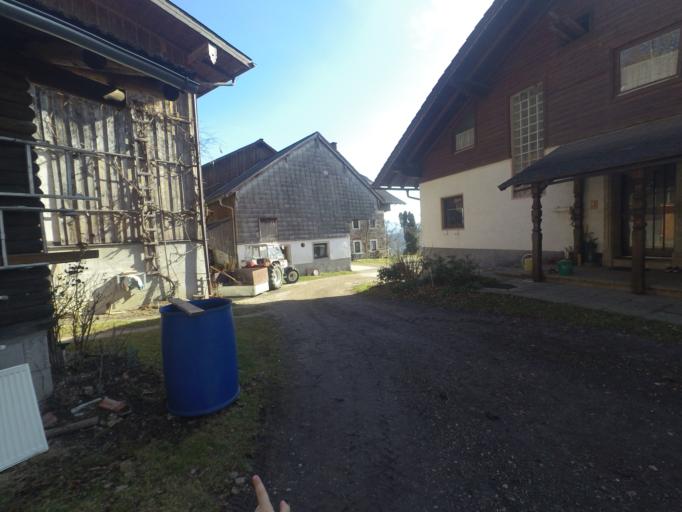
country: AT
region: Salzburg
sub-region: Politischer Bezirk Salzburg-Umgebung
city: Bergheim
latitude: 47.8526
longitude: 13.0365
